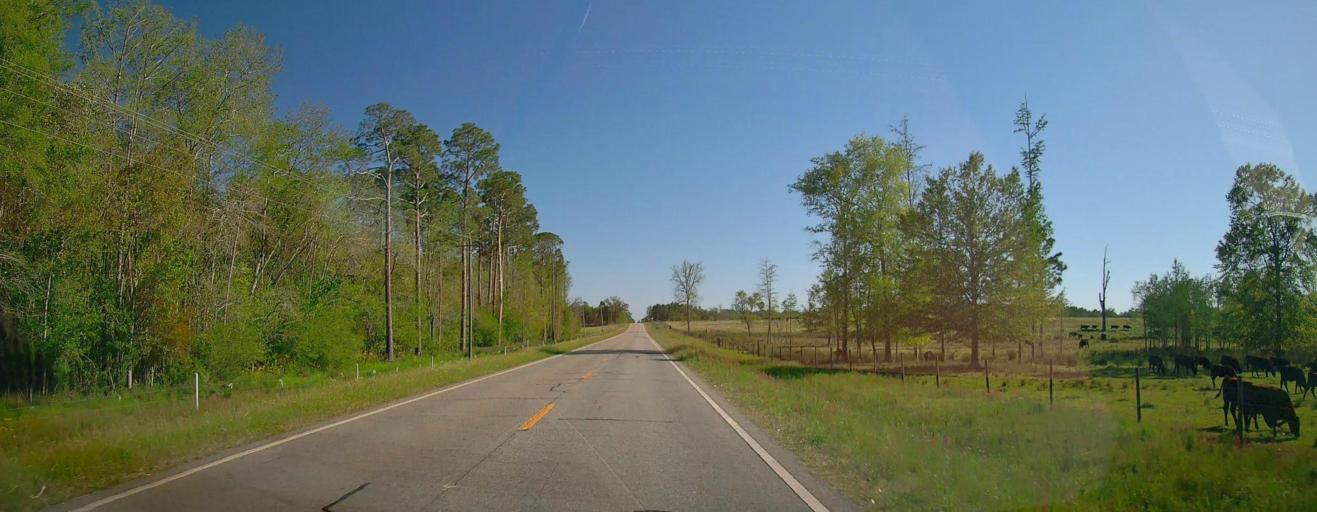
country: US
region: Georgia
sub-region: Wilcox County
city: Rochelle
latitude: 31.8516
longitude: -83.4890
